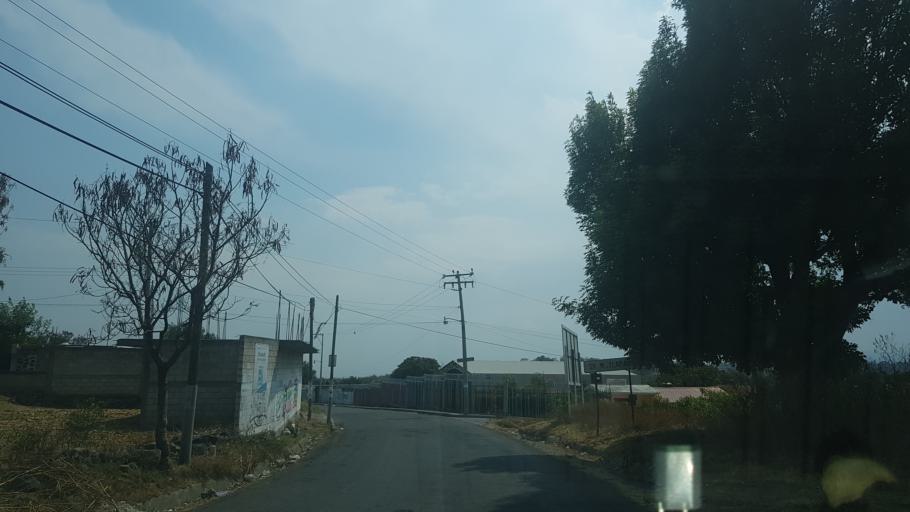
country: MX
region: Puebla
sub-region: Tianguismanalco
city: San Martin Tlapala
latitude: 18.9676
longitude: -98.4571
